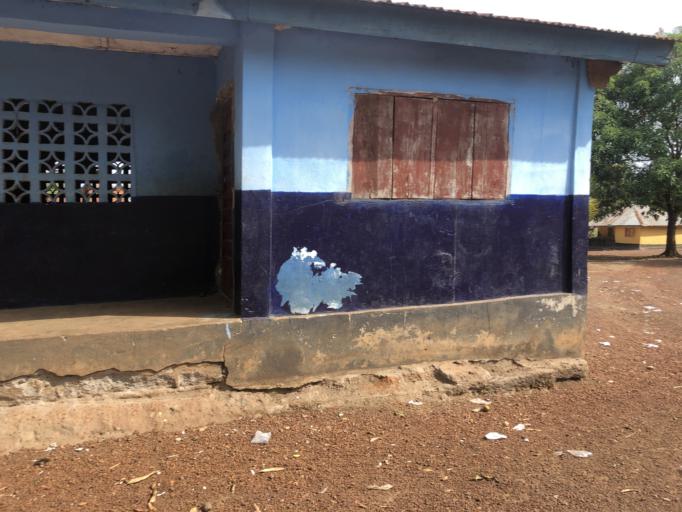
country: SL
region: Northern Province
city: Yonibana
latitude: 8.4713
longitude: -12.2189
